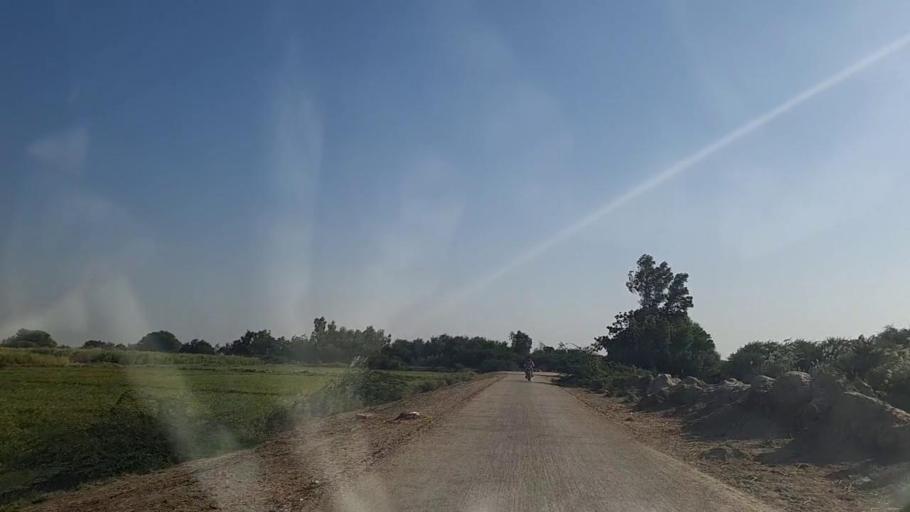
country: PK
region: Sindh
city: Mirpur Batoro
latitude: 24.5546
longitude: 68.1722
